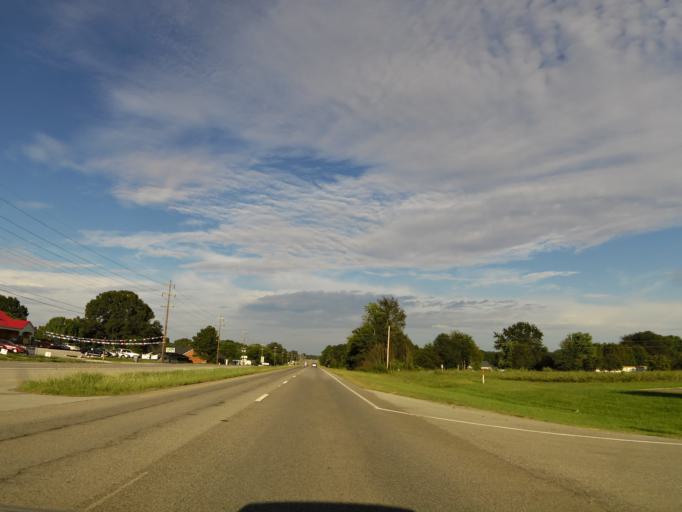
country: US
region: Alabama
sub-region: Lauderdale County
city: Killen
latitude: 34.8605
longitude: -87.4694
